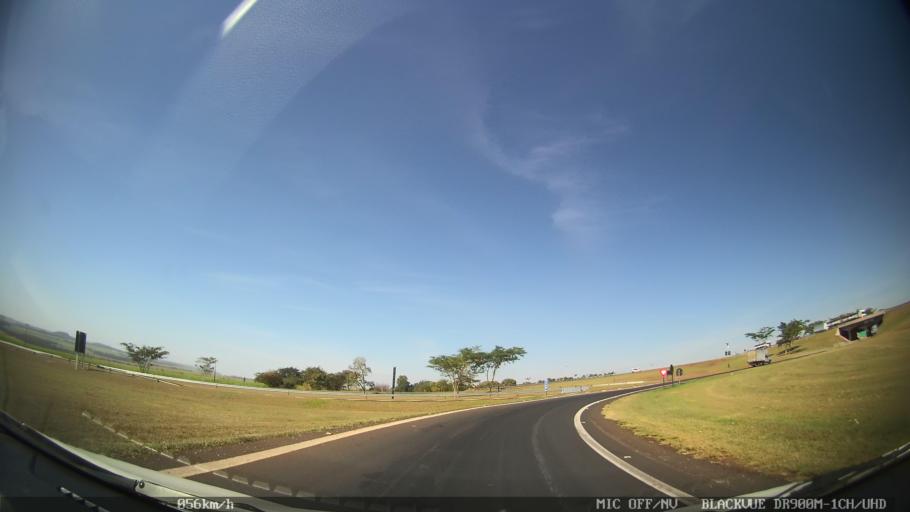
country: BR
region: Sao Paulo
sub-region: Jardinopolis
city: Jardinopolis
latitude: -21.0916
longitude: -47.7942
